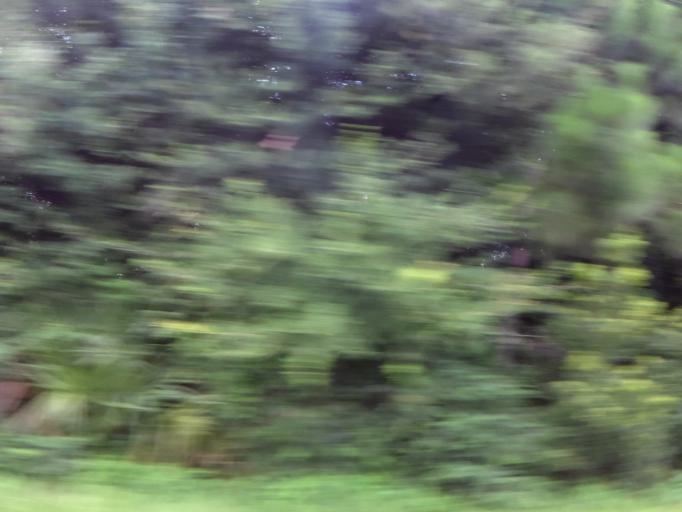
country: US
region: Florida
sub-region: Duval County
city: Jacksonville
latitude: 30.3201
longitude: -81.7587
